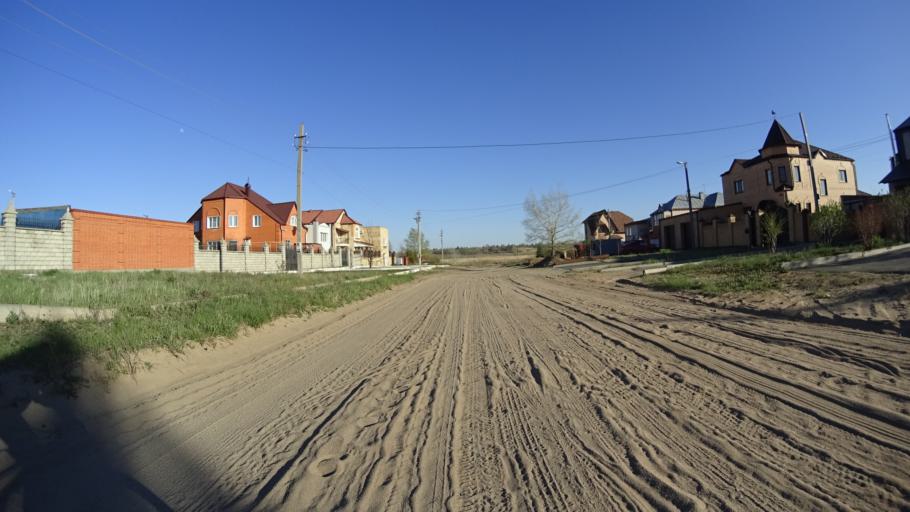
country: RU
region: Chelyabinsk
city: Troitsk
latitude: 54.0702
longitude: 61.5372
